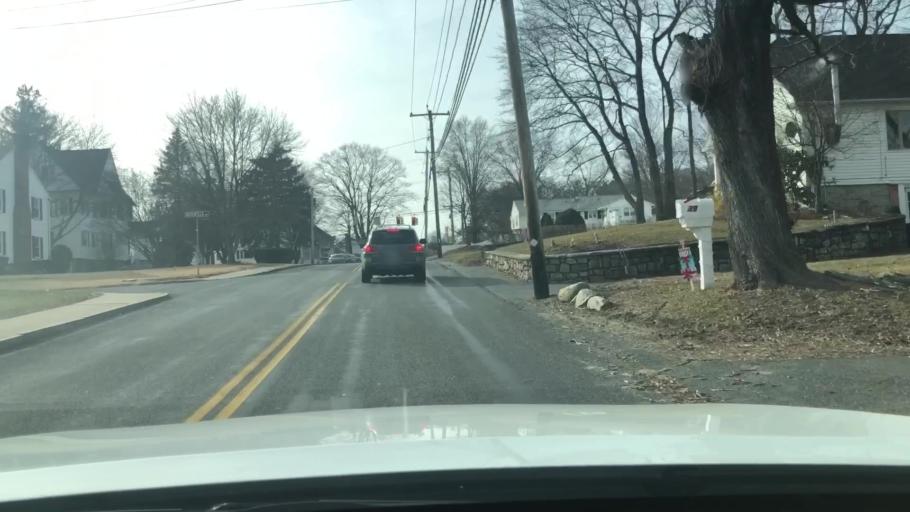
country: US
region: Massachusetts
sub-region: Worcester County
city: Milford
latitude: 42.1524
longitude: -71.5272
